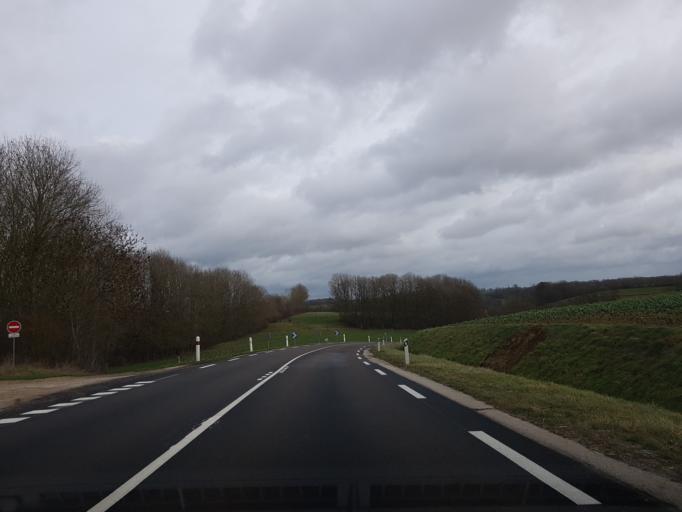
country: FR
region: Champagne-Ardenne
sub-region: Departement de la Haute-Marne
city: Langres
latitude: 47.8575
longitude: 5.3567
